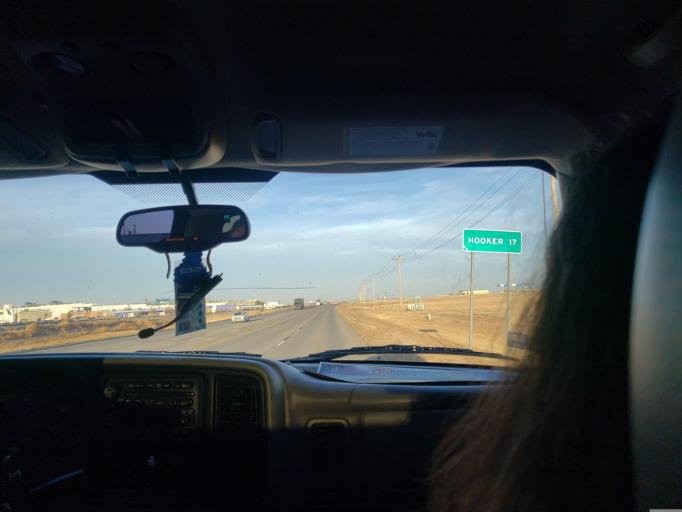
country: US
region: Oklahoma
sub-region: Texas County
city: Guymon
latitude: 36.7041
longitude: -101.4474
